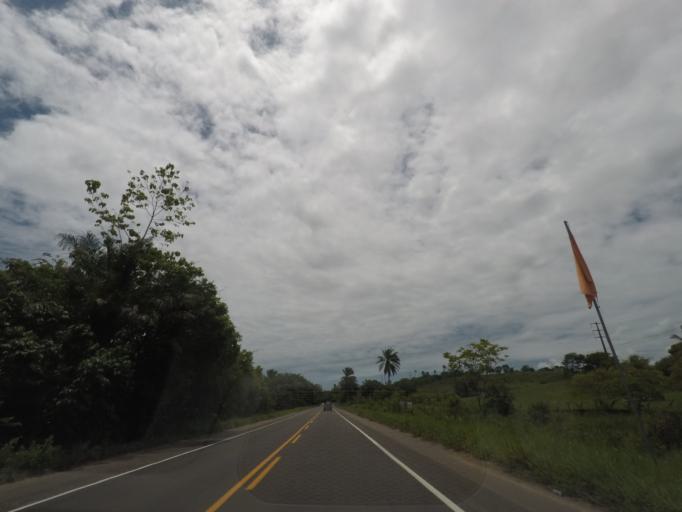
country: BR
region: Bahia
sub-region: Itaparica
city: Itaparica
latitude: -12.9616
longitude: -38.6336
